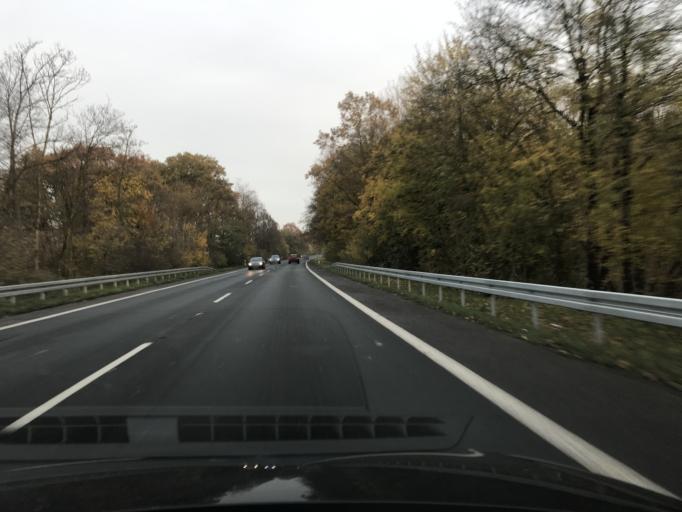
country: DE
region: North Rhine-Westphalia
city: Werne
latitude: 51.7009
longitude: 7.6829
